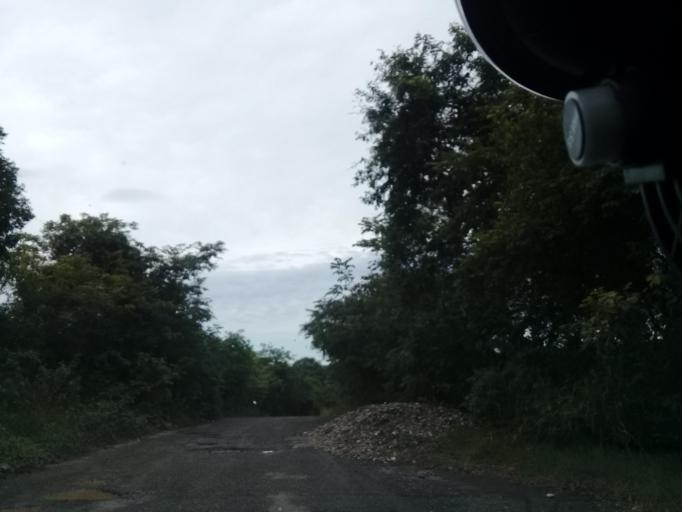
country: MX
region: Hidalgo
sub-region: Huejutla de Reyes
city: Chalahuiyapa
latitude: 21.2017
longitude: -98.3516
